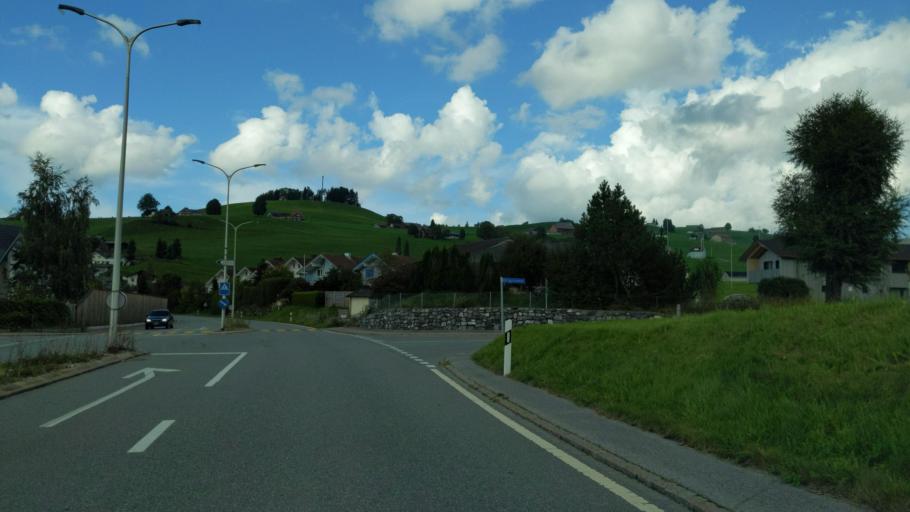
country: CH
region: Appenzell Innerrhoden
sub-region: Appenzell Inner Rhodes
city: Appenzell
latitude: 47.3274
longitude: 9.4269
